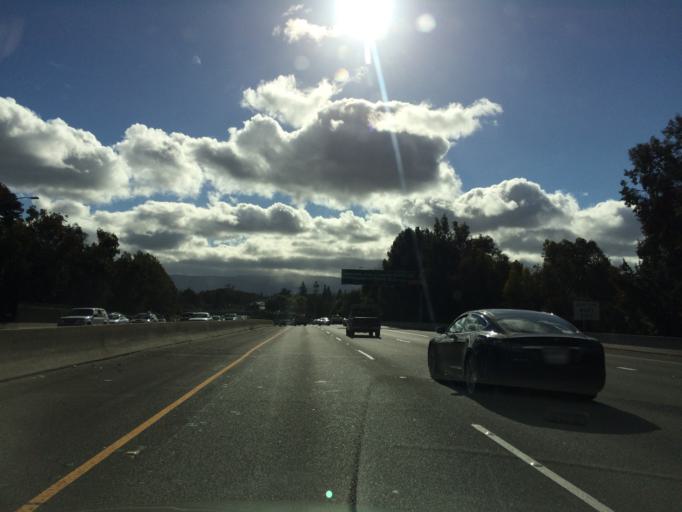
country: US
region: California
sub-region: Santa Clara County
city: Burbank
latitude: 37.3457
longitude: -121.9227
